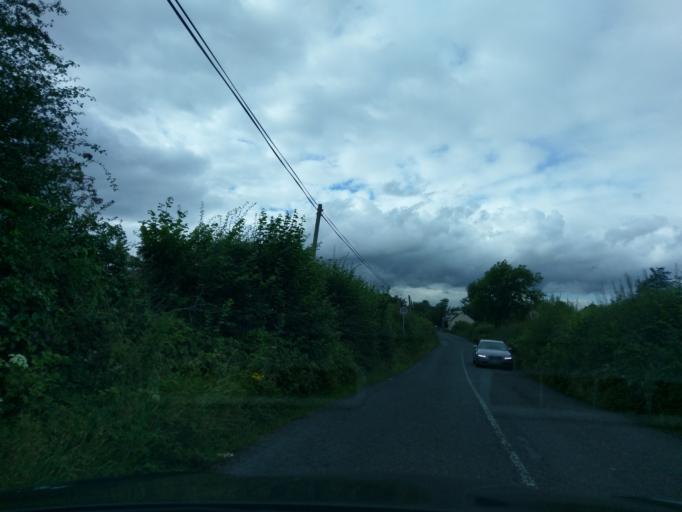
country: IE
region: Connaught
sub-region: County Galway
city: Athenry
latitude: 53.2384
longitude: -8.7457
